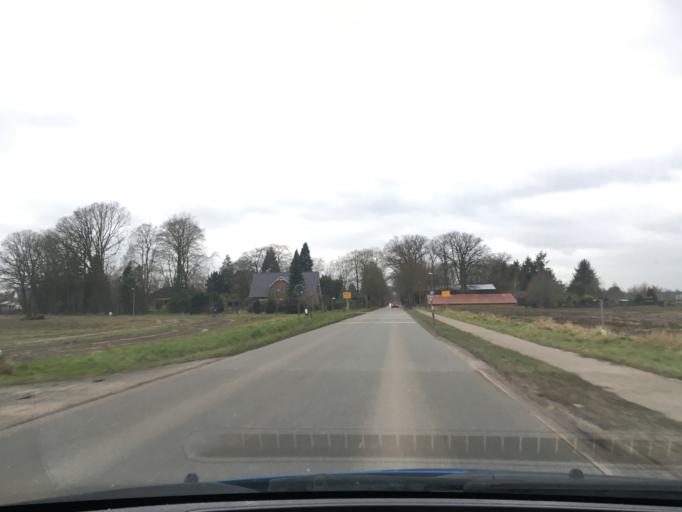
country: DE
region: Lower Saxony
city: Radbruch
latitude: 53.3071
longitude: 10.3027
